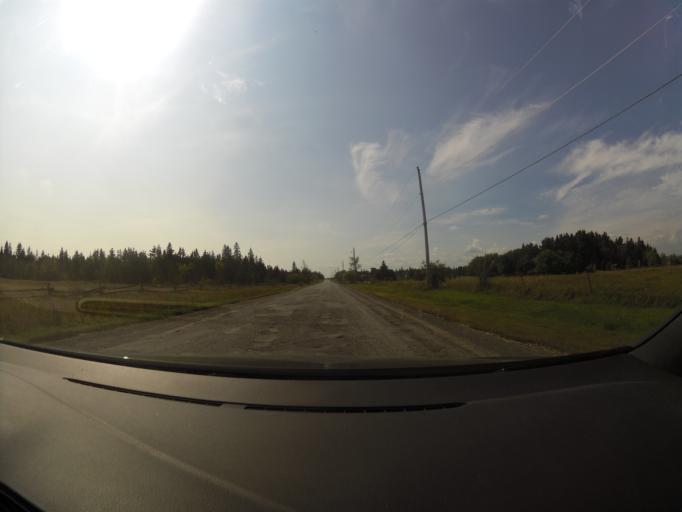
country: CA
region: Ontario
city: Carleton Place
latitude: 45.3006
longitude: -76.2148
